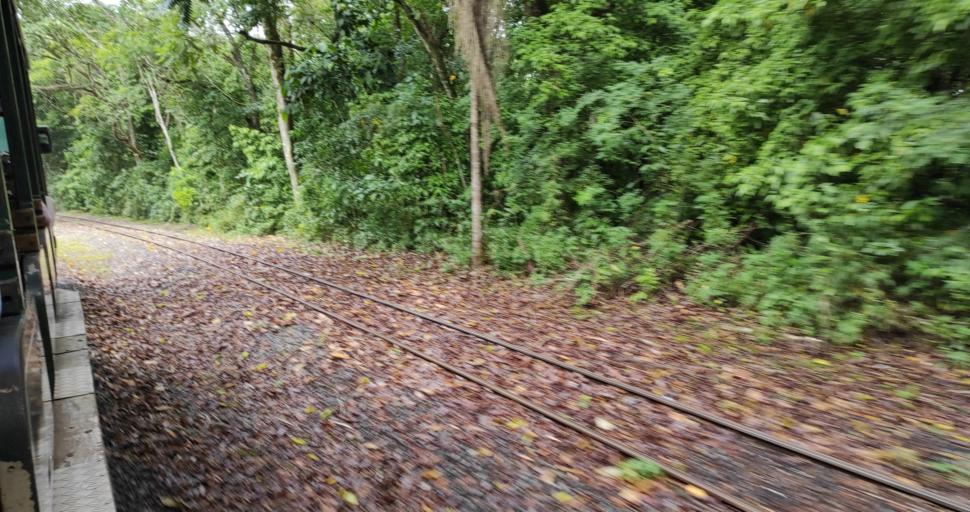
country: AR
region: Misiones
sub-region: Departamento de Iguazu
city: Puerto Iguazu
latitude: -25.6804
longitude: -54.4496
